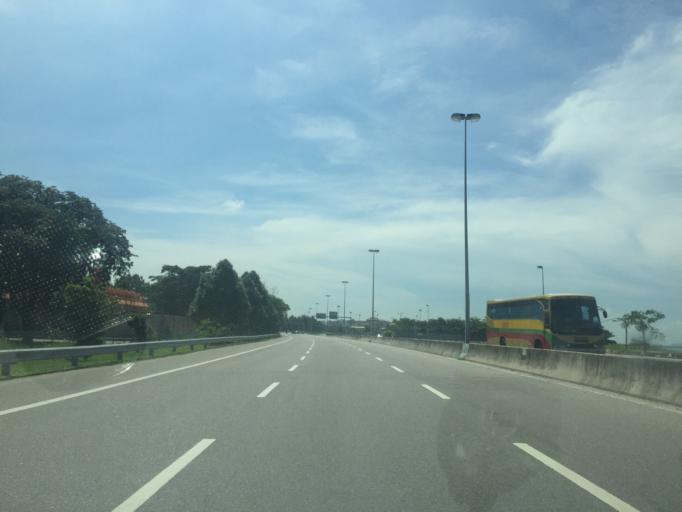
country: MY
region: Penang
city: Permatang Kuching
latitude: 5.4381
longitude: 100.3783
